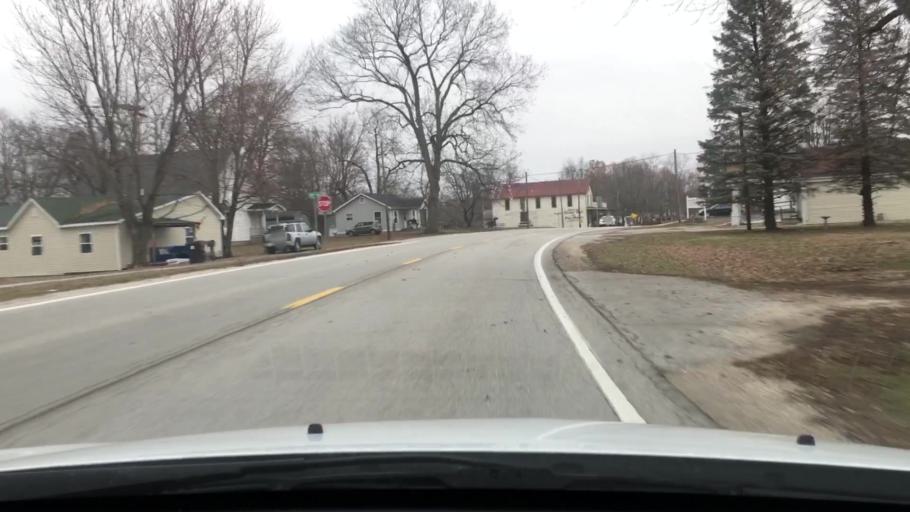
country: US
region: Illinois
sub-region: Pike County
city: Pittsfield
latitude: 39.5451
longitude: -90.9201
